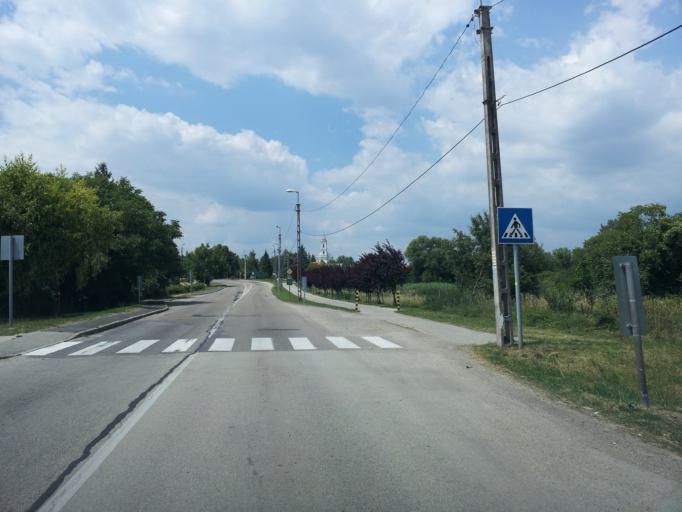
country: HU
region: Veszprem
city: Balatonfured
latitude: 46.9268
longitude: 17.8368
